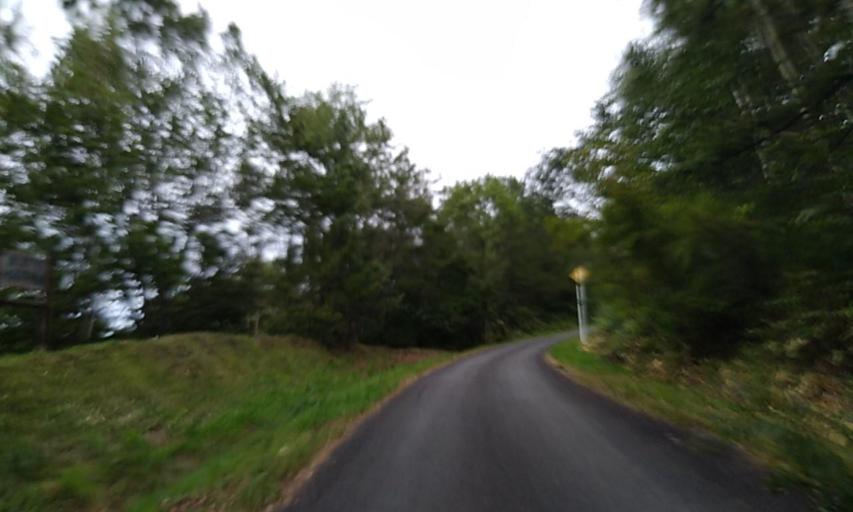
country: JP
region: Hokkaido
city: Obihiro
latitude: 42.8265
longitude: 142.9827
